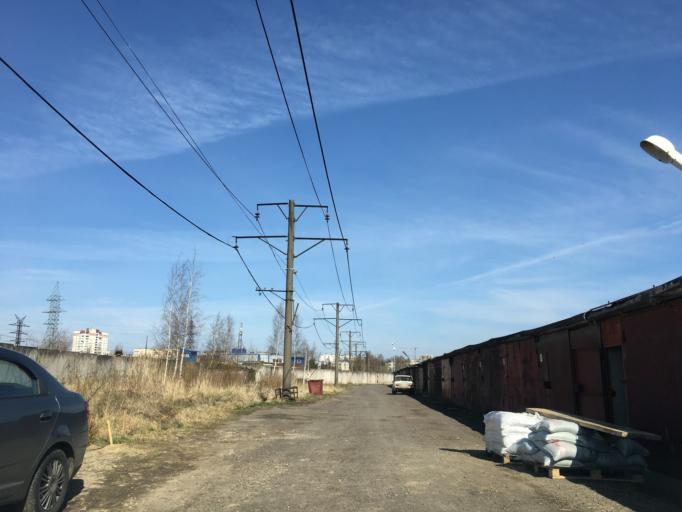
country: RU
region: St.-Petersburg
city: Sosnovaya Polyana
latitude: 59.8212
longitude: 30.1625
